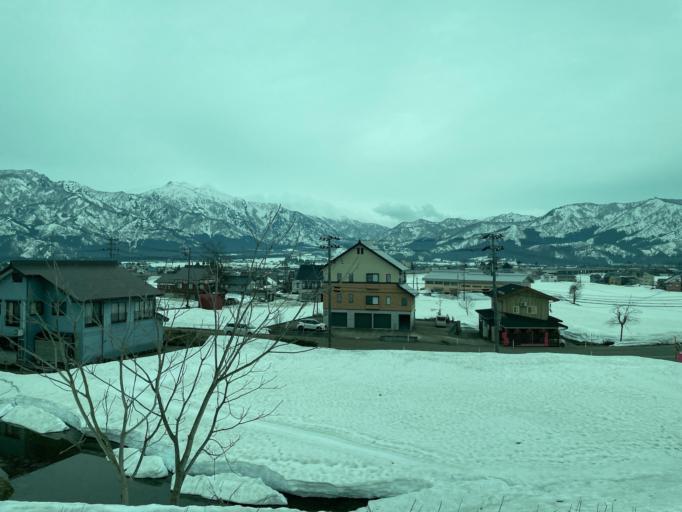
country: JP
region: Niigata
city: Shiozawa
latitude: 37.0344
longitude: 138.8367
